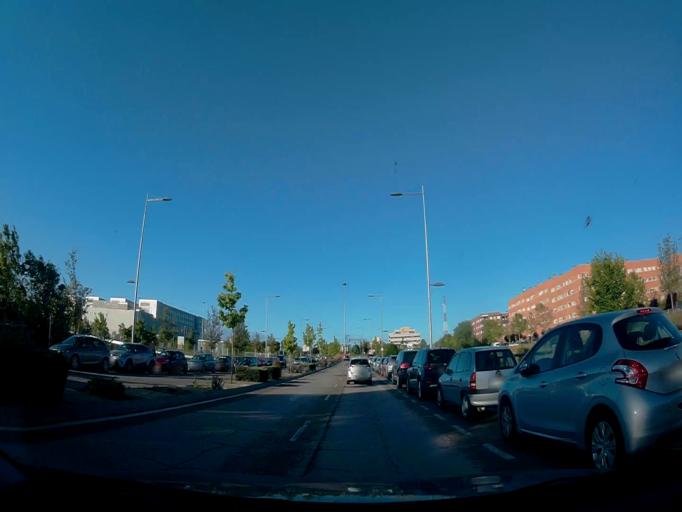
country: ES
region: Madrid
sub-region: Provincia de Madrid
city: San Sebastian de los Reyes
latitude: 40.5612
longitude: -3.6103
